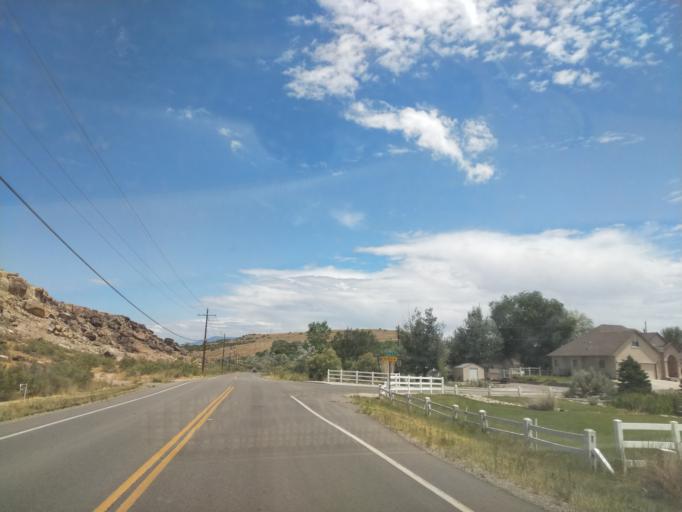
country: US
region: Colorado
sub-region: Mesa County
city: Redlands
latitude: 39.0727
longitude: -108.6468
